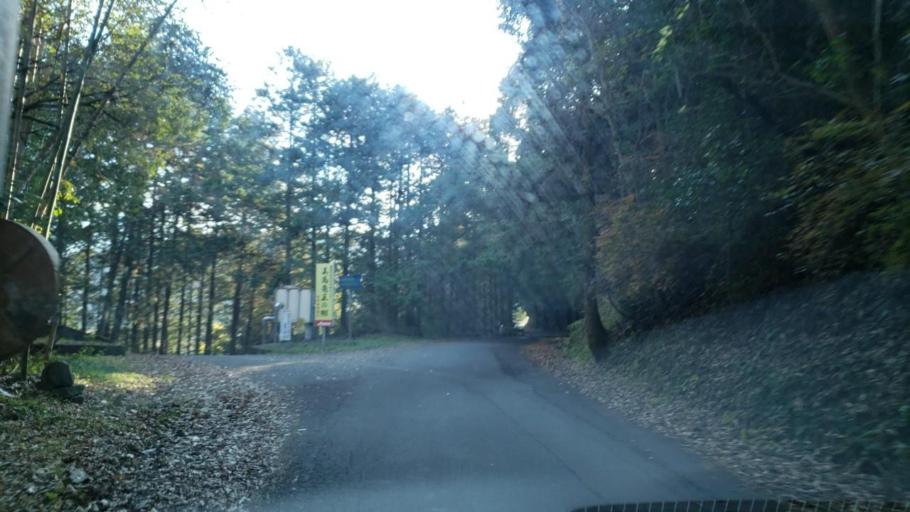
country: JP
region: Tokushima
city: Wakimachi
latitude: 34.0987
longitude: 134.0682
